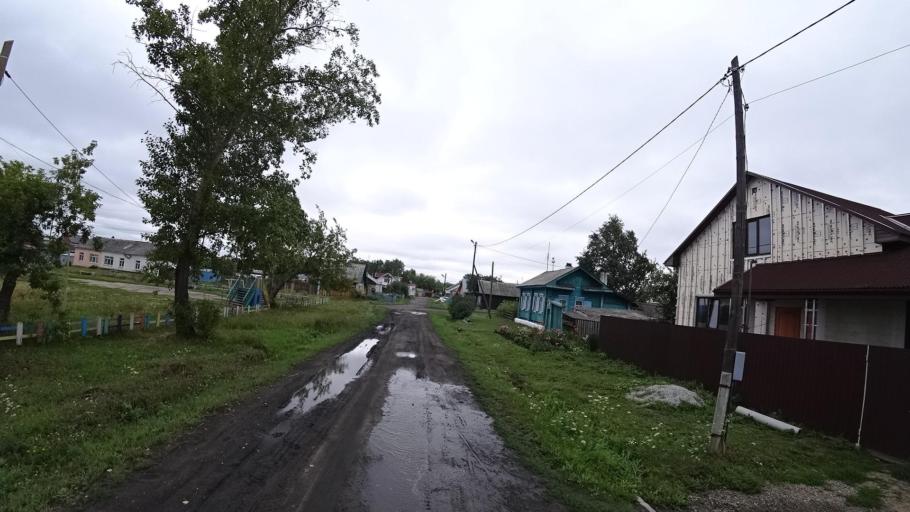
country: RU
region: Sverdlovsk
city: Kamyshlov
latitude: 56.8479
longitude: 62.7644
